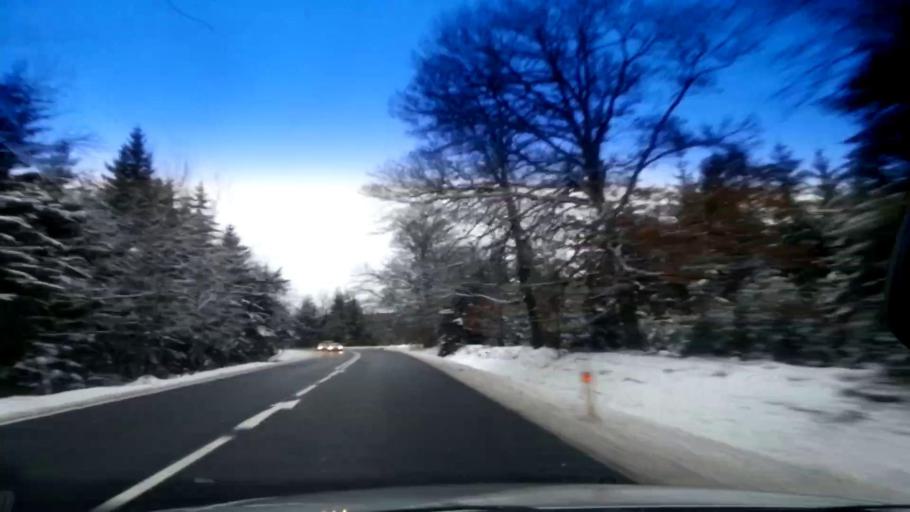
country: CZ
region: Karlovarsky
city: Hazlov
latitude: 50.1867
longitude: 12.2409
